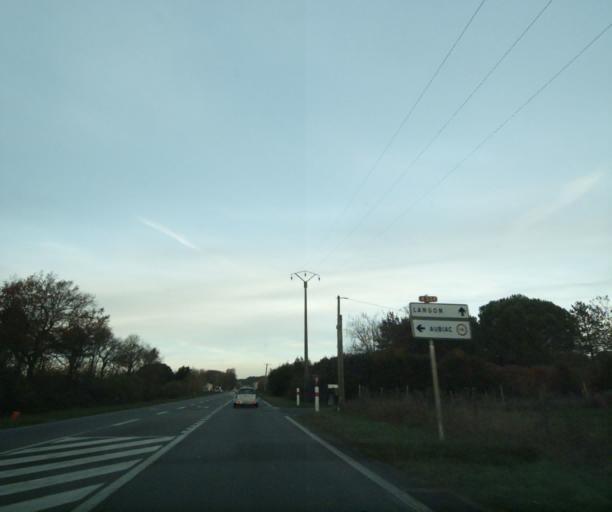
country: FR
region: Aquitaine
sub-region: Departement de la Gironde
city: Bazas
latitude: 44.4661
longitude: -0.2299
